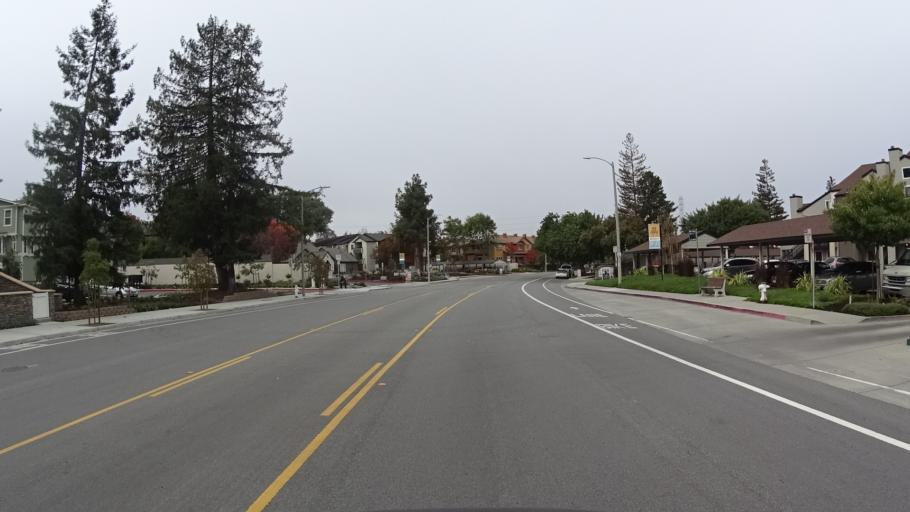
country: US
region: California
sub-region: Santa Clara County
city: Sunnyvale
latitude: 37.3708
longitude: -122.0149
